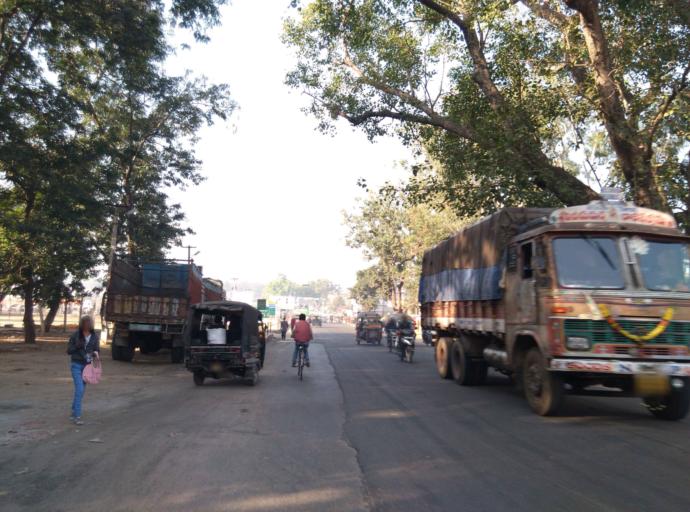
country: IN
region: Jharkhand
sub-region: Ranchi
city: Ranchi
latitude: 23.3890
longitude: 85.3763
